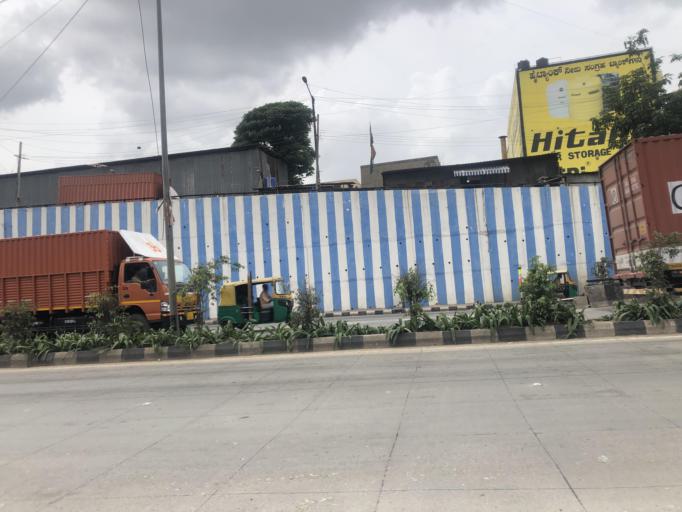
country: IN
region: Karnataka
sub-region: Bangalore Urban
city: Bangalore
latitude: 12.9457
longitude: 77.5272
